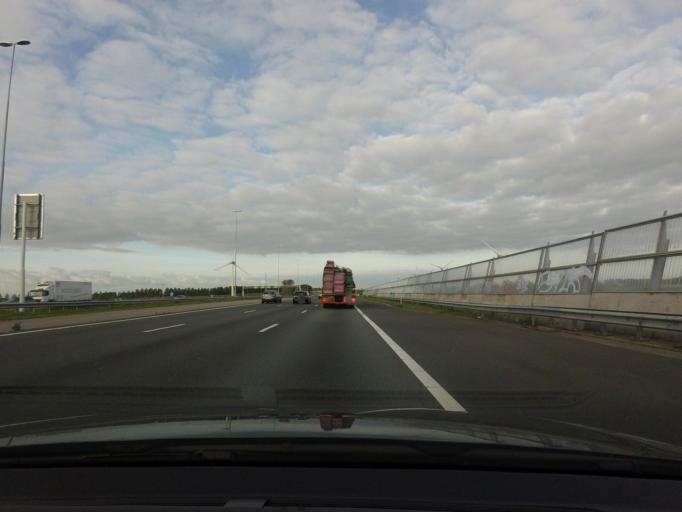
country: NL
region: South Holland
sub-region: Gemeente Kaag en Braassem
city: Oude Wetering
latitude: 52.2262
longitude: 4.6387
